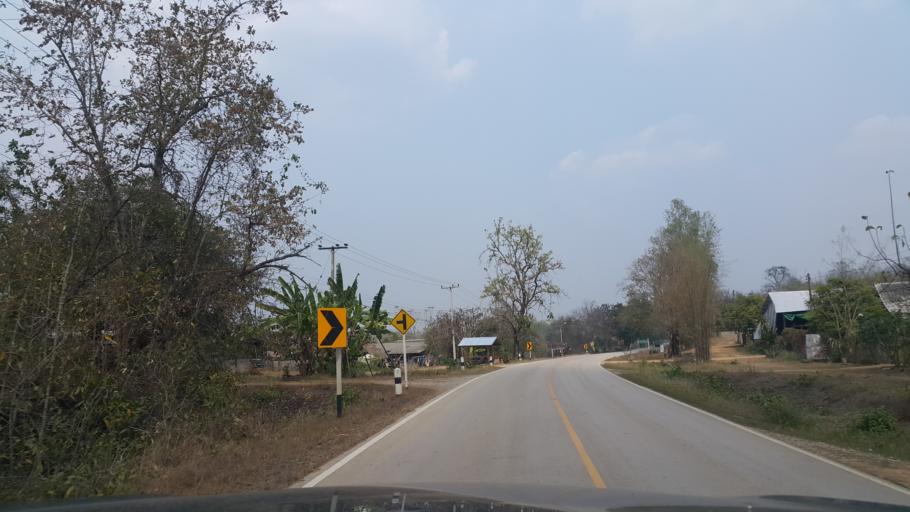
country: TH
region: Lampang
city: Soem Ngam
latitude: 17.9933
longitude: 99.1707
